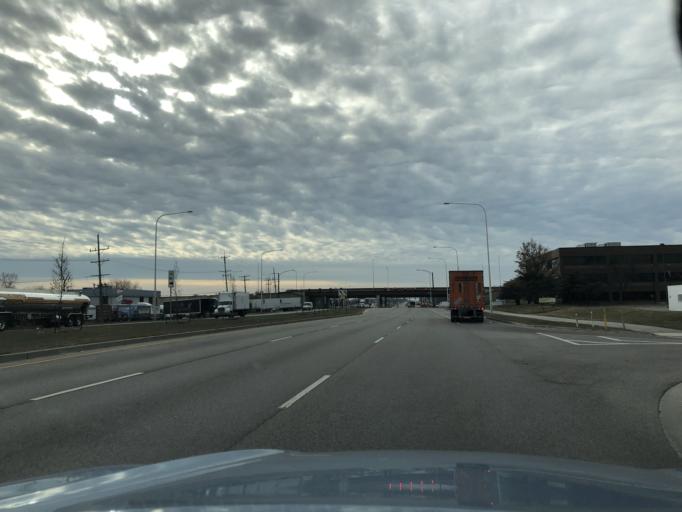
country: US
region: Illinois
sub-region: Cook County
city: Elk Grove Village
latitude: 41.9855
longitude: -87.9595
